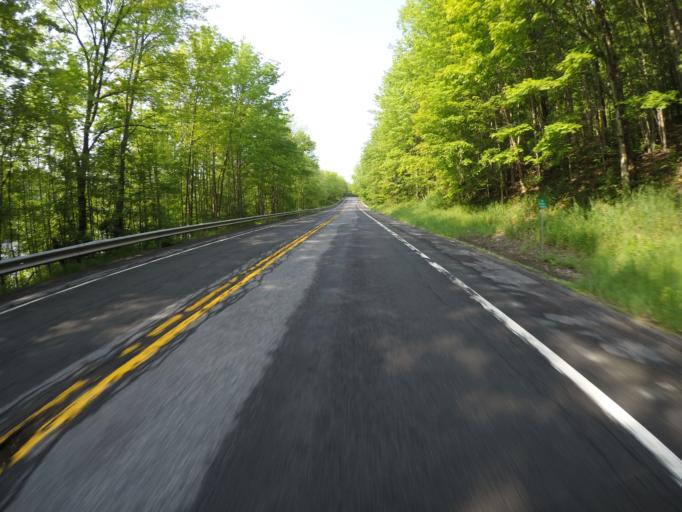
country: US
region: New York
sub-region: Delaware County
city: Delhi
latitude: 42.1141
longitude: -74.7729
